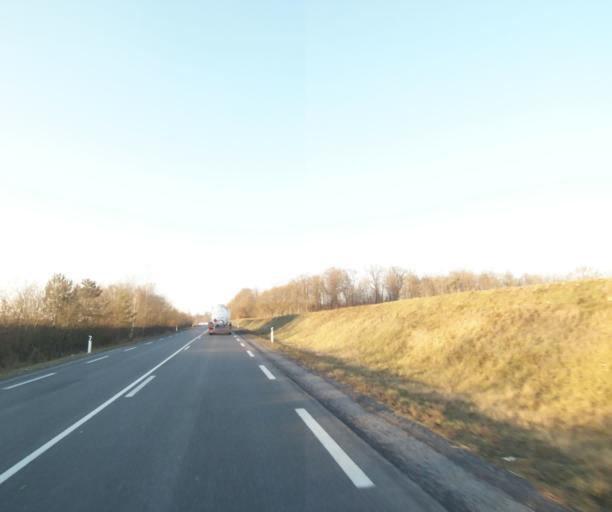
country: FR
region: Champagne-Ardenne
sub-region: Departement de la Haute-Marne
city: Bienville
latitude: 48.5491
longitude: 5.0655
